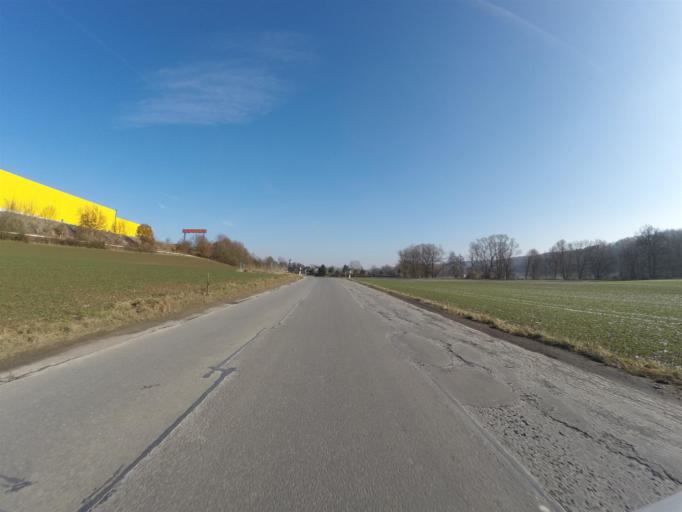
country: DE
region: Thuringia
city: Sulza
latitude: 50.8750
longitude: 11.6122
